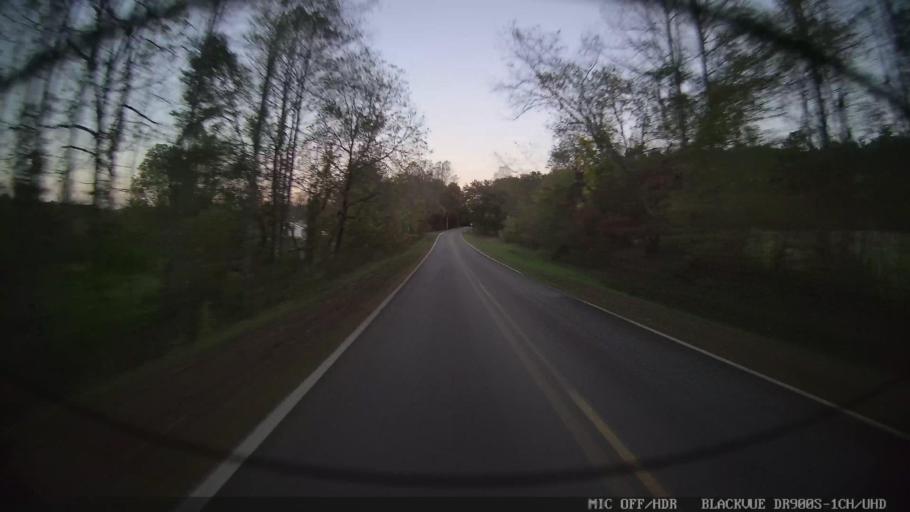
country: US
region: North Carolina
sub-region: Clay County
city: Hayesville
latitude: 34.9639
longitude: -83.8888
